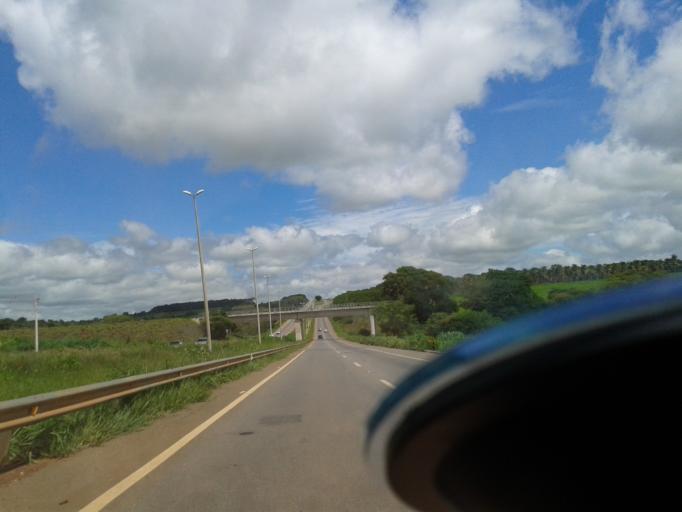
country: BR
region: Goias
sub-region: Goianira
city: Goianira
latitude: -16.4803
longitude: -49.4311
